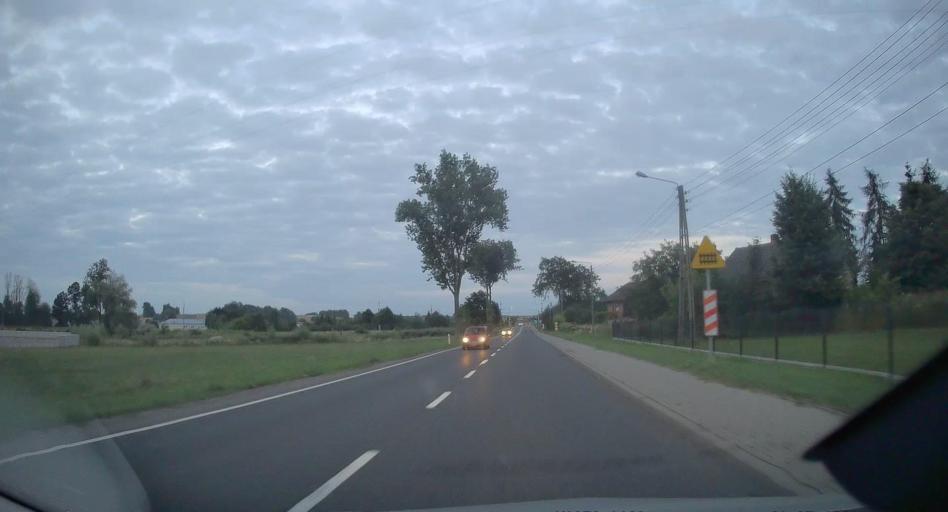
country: PL
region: Silesian Voivodeship
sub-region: Powiat klobucki
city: Starokrzepice
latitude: 51.0269
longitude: 18.6409
